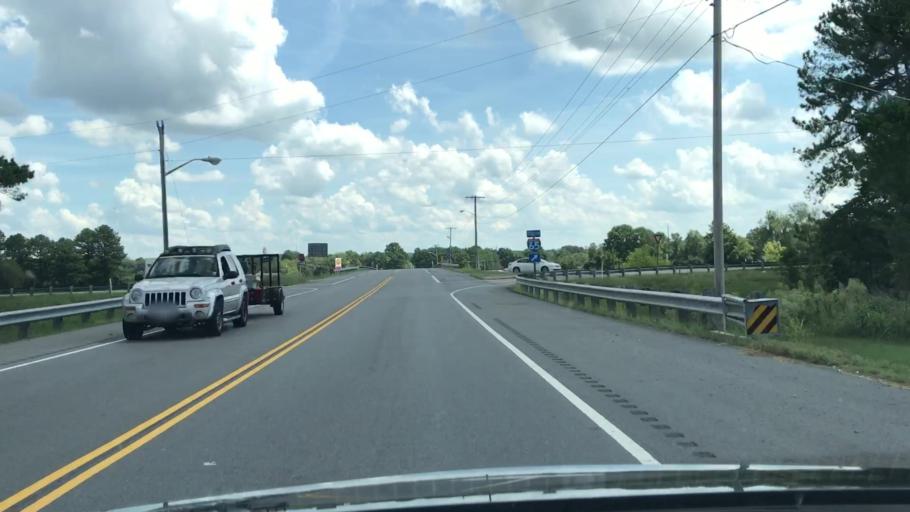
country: US
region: Tennessee
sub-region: Robertson County
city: Cross Plains
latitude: 36.5283
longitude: -86.6448
